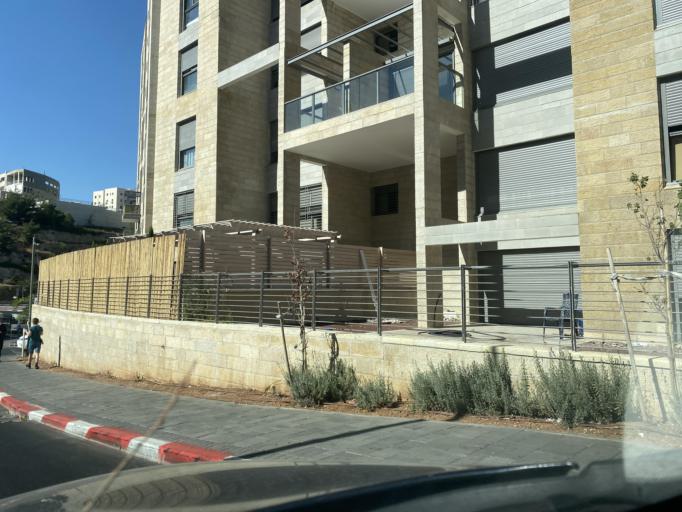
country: PS
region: West Bank
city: Bayt Iksa
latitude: 31.8177
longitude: 35.1938
